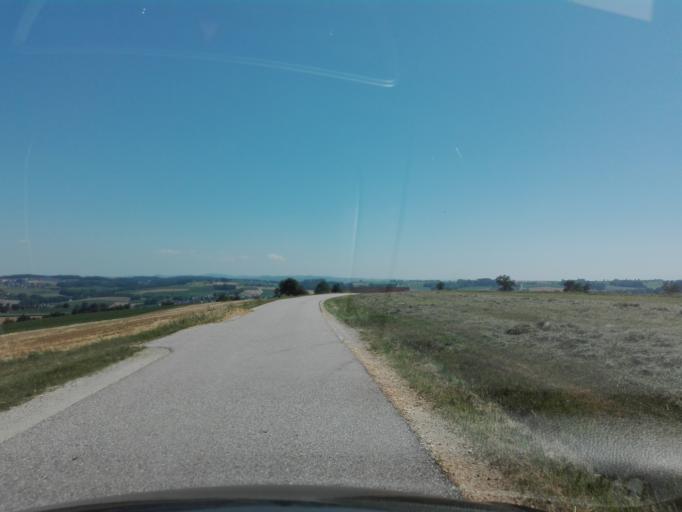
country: AT
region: Upper Austria
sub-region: Politischer Bezirk Urfahr-Umgebung
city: Engerwitzdorf
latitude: 48.2962
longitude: 14.4534
